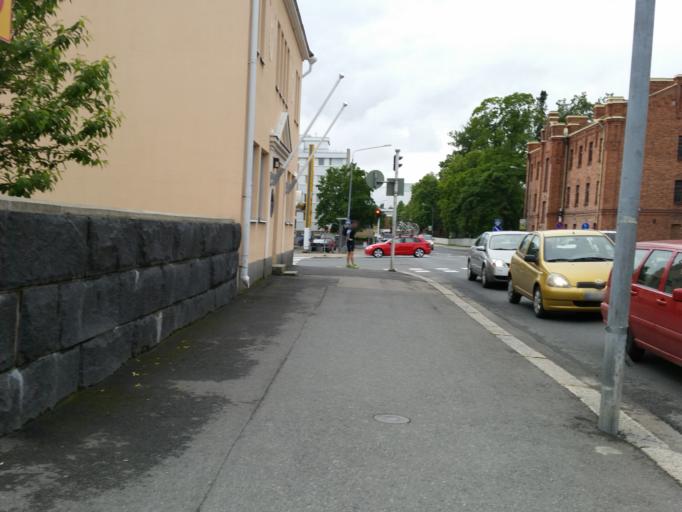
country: FI
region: Northern Savo
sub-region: Kuopio
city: Kuopio
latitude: 62.8929
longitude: 27.6722
